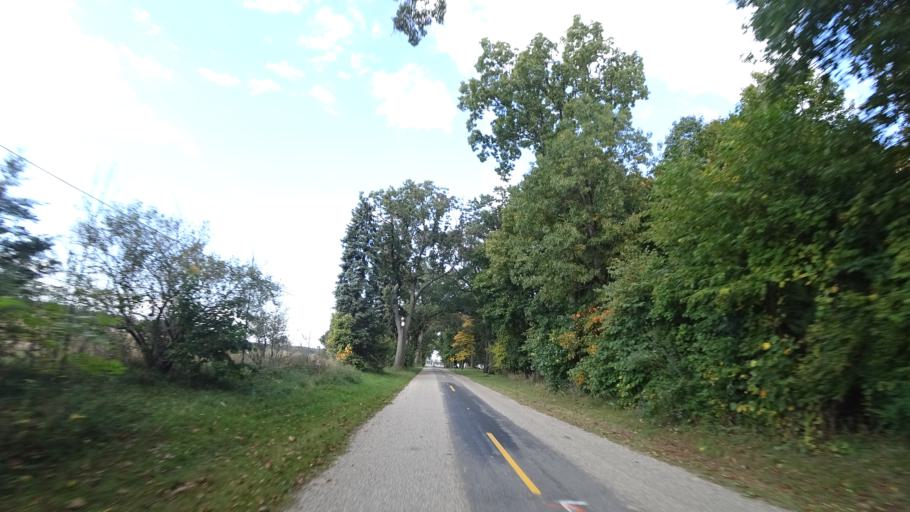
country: US
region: Michigan
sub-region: Saint Joseph County
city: Three Rivers
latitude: 41.9526
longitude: -85.5910
